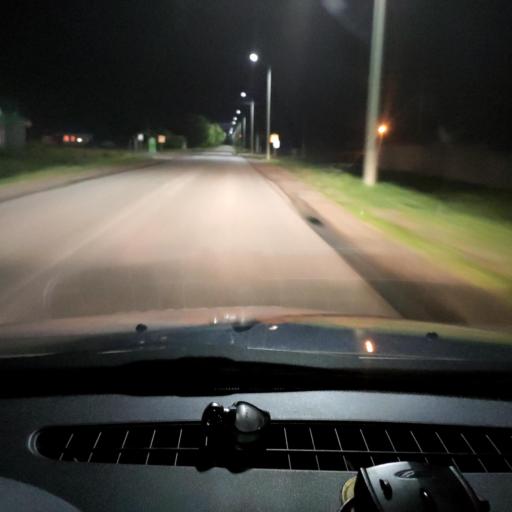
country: RU
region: Voronezj
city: Khrenovoye
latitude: 51.1148
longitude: 40.2656
